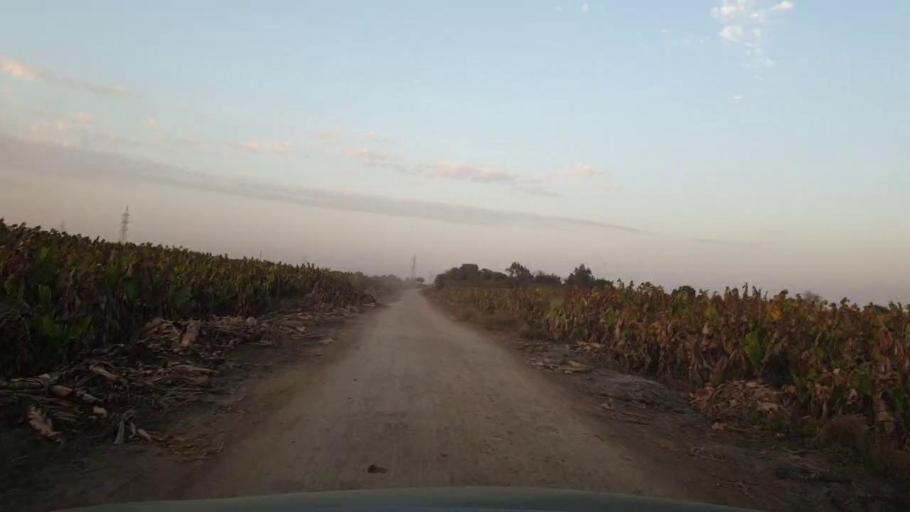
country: PK
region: Sindh
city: Matiari
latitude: 25.6121
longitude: 68.4832
